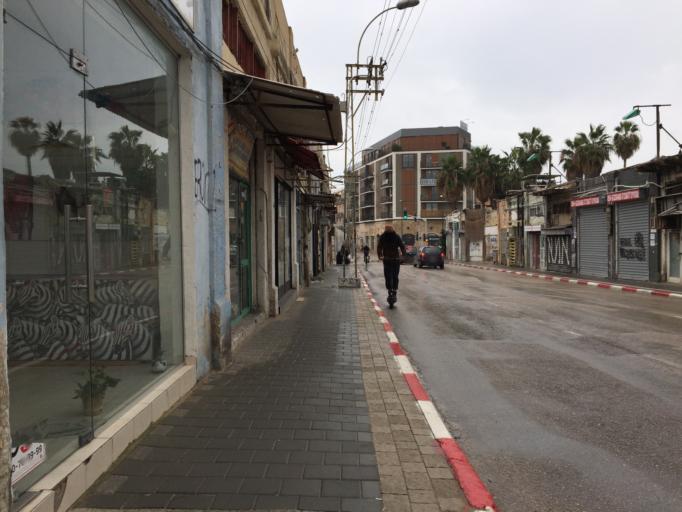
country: IL
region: Tel Aviv
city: Yafo
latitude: 32.0570
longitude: 34.7609
